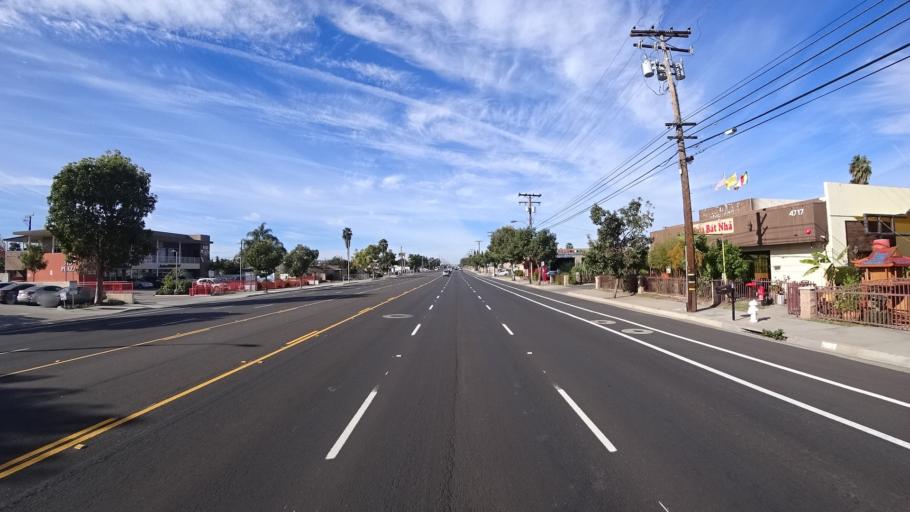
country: US
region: California
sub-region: Orange County
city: Garden Grove
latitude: 33.7452
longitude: -117.9316
